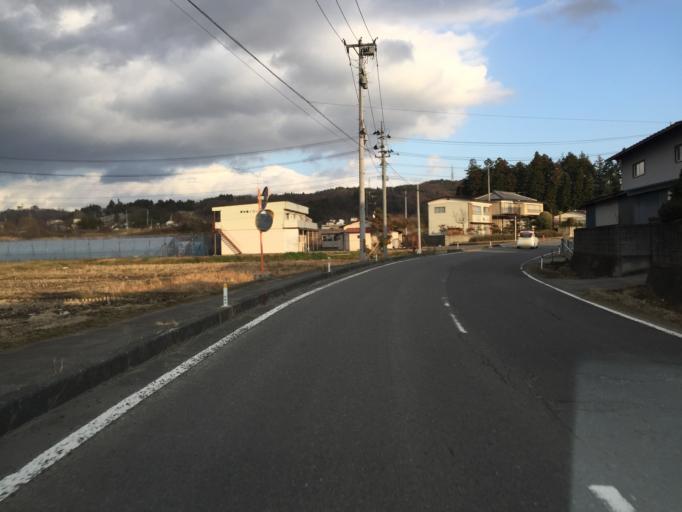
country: JP
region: Fukushima
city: Motomiya
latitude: 37.5069
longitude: 140.4049
